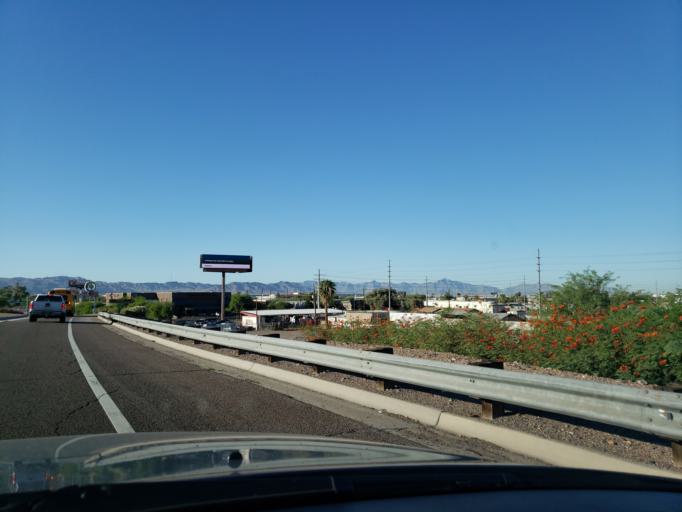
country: US
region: Arizona
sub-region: Maricopa County
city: Phoenix
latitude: 33.4512
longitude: -112.0381
